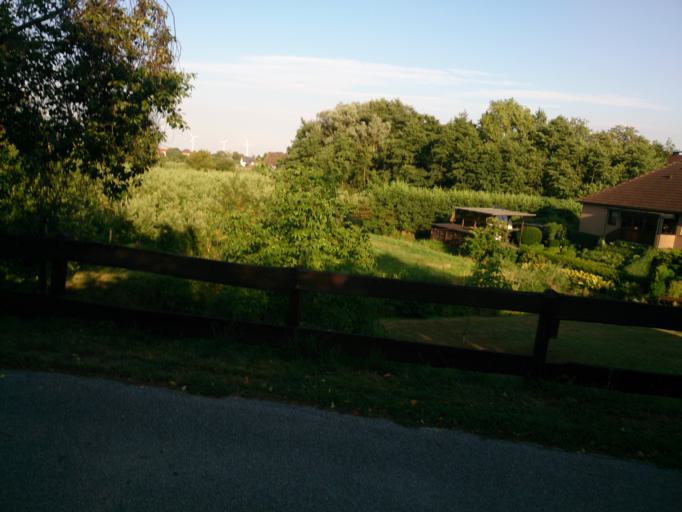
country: DE
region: Lower Saxony
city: Neu Wulmstorf
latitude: 53.5290
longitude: 9.8490
